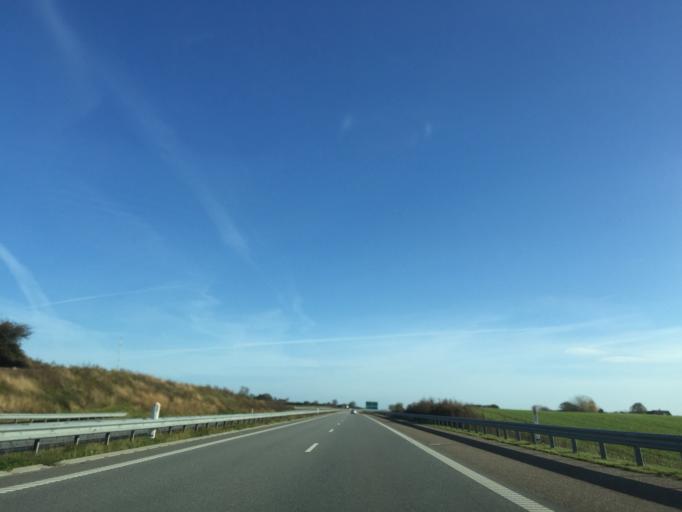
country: DK
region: South Denmark
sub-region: Sonderborg Kommune
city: Grasten
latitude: 54.9551
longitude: 9.5334
